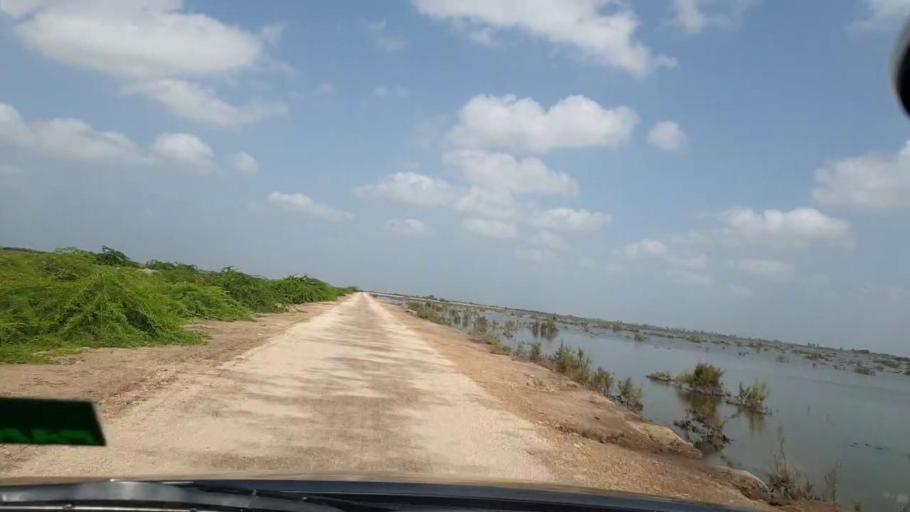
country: PK
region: Sindh
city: Kadhan
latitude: 24.5787
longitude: 69.1421
